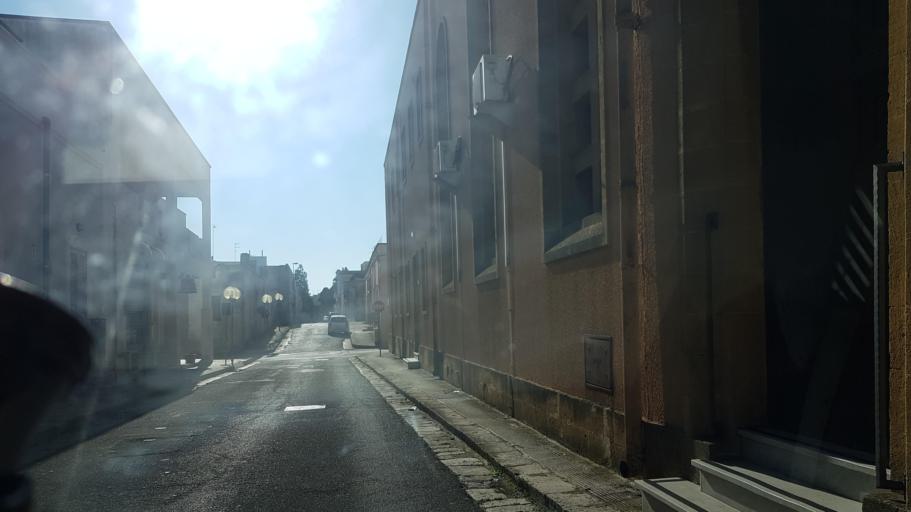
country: IT
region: Apulia
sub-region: Provincia di Lecce
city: Squinzano
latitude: 40.4342
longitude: 18.0452
